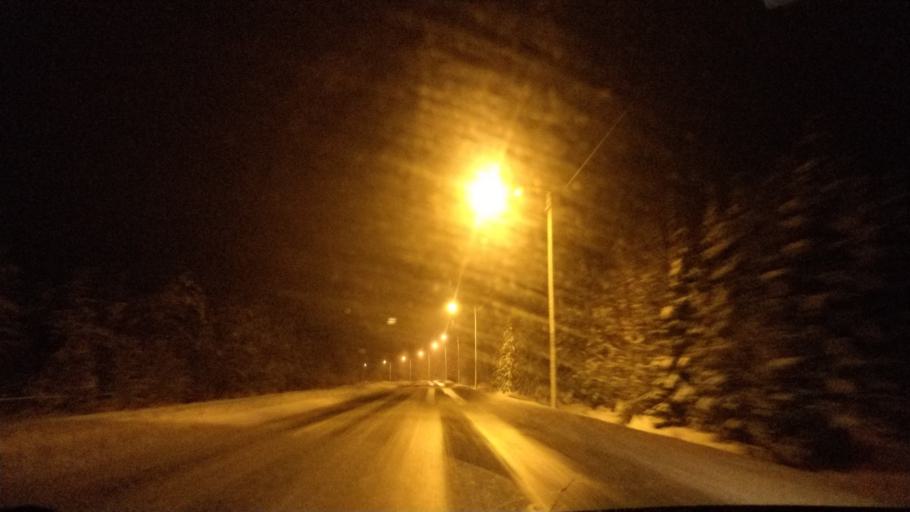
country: FI
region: Lapland
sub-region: Rovaniemi
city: Rovaniemi
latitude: 66.4057
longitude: 25.3947
